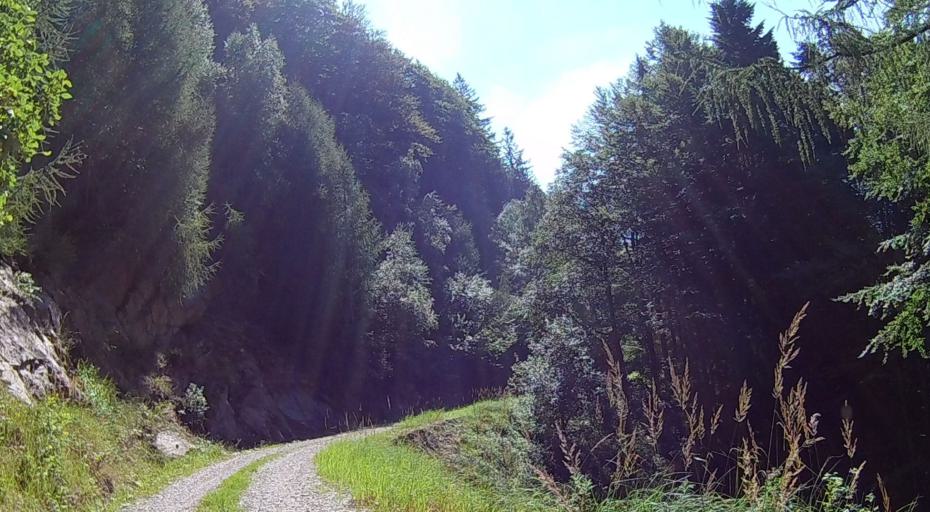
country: SI
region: Selnica ob Dravi
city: Selnica ob Dravi
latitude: 46.4958
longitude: 15.4626
